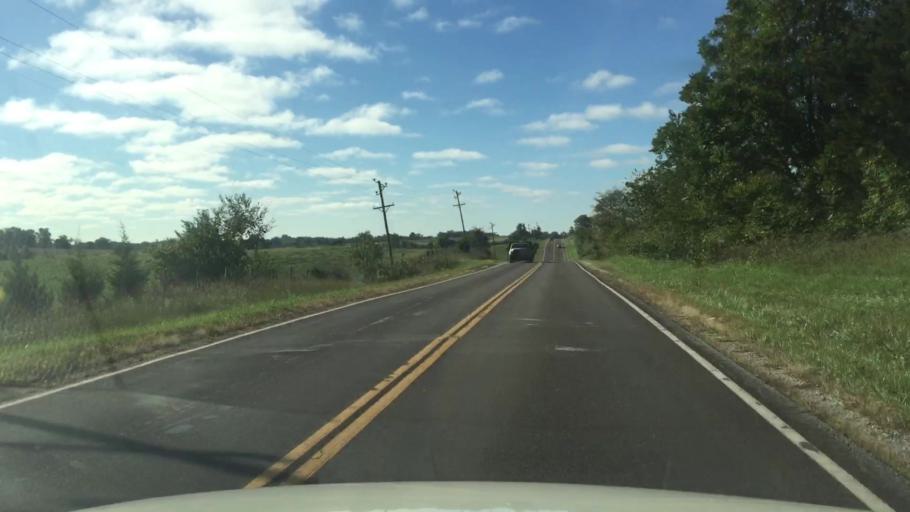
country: US
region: Missouri
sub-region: Howard County
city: New Franklin
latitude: 39.0806
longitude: -92.7456
